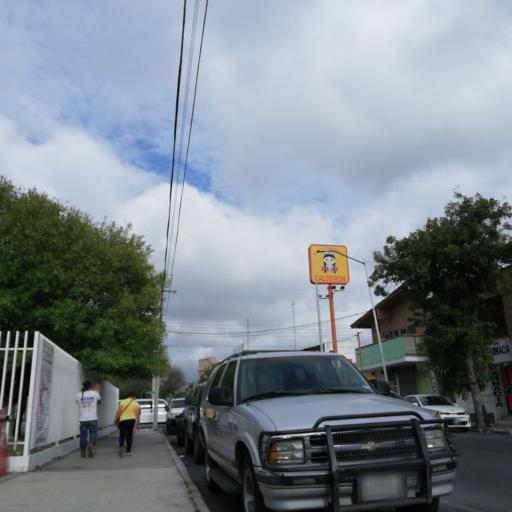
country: MX
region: Tamaulipas
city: Nuevo Laredo
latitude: 27.4860
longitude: -99.5043
